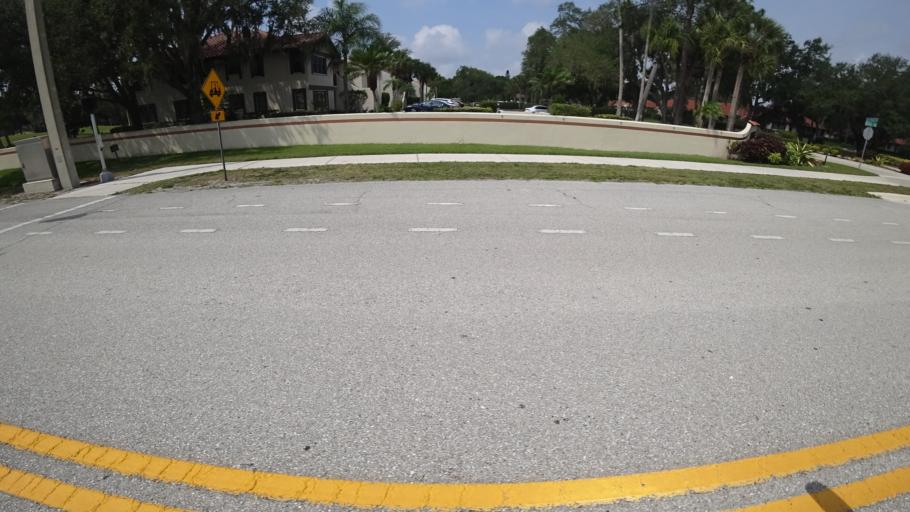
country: US
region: Florida
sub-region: Sarasota County
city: Desoto Lakes
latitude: 27.4112
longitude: -82.4891
